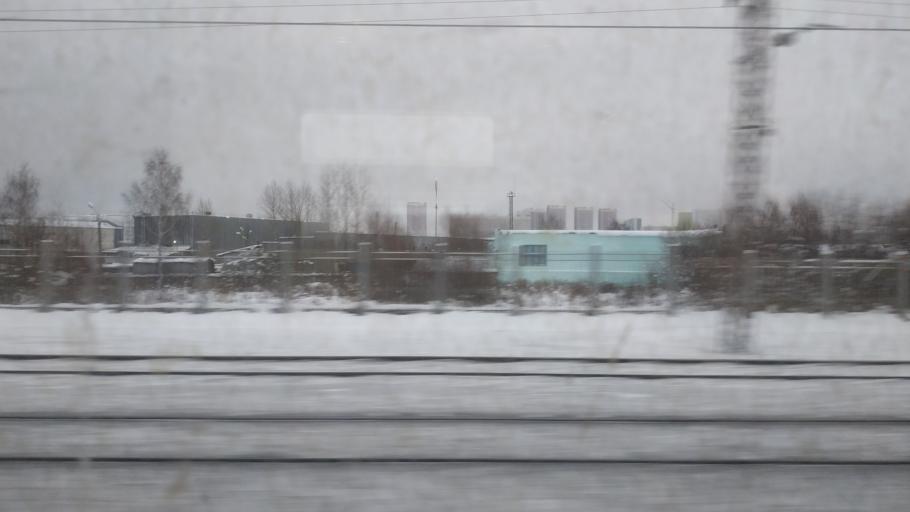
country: RU
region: Moskovskaya
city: Shcherbinka
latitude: 55.5320
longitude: 37.5685
